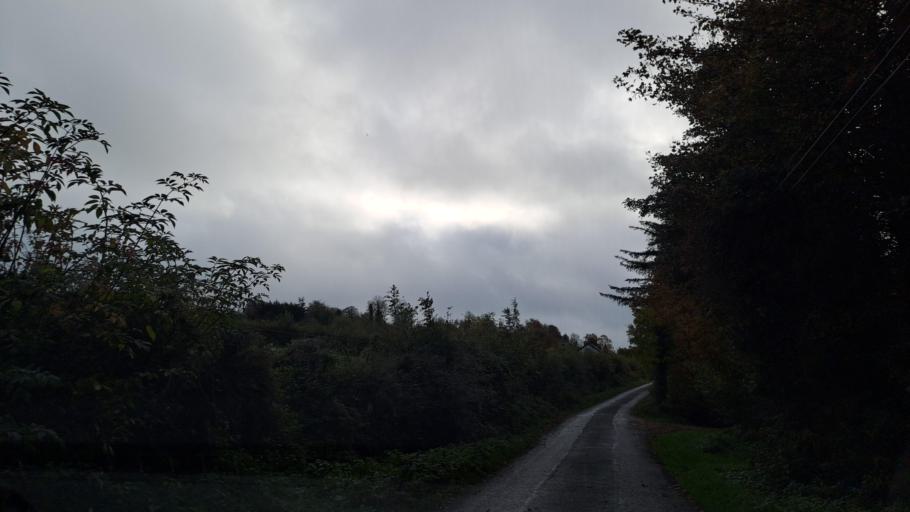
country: IE
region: Ulster
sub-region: An Cabhan
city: Bailieborough
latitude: 53.9886
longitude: -7.0143
